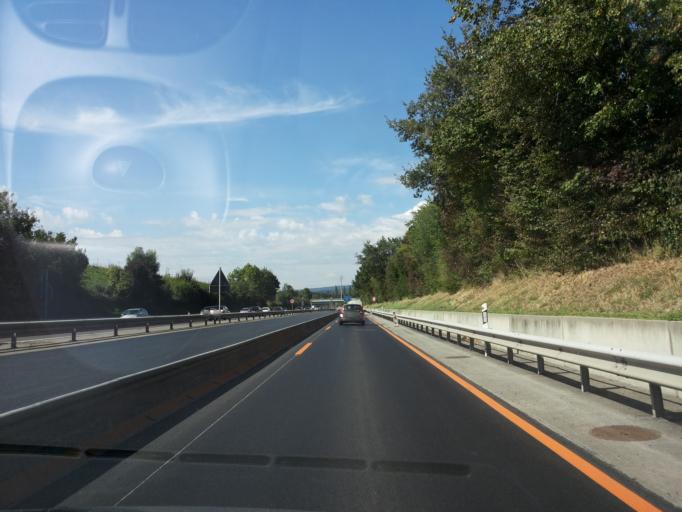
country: CH
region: Lucerne
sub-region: Sursee District
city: Sursee
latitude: 47.1773
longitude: 8.1213
